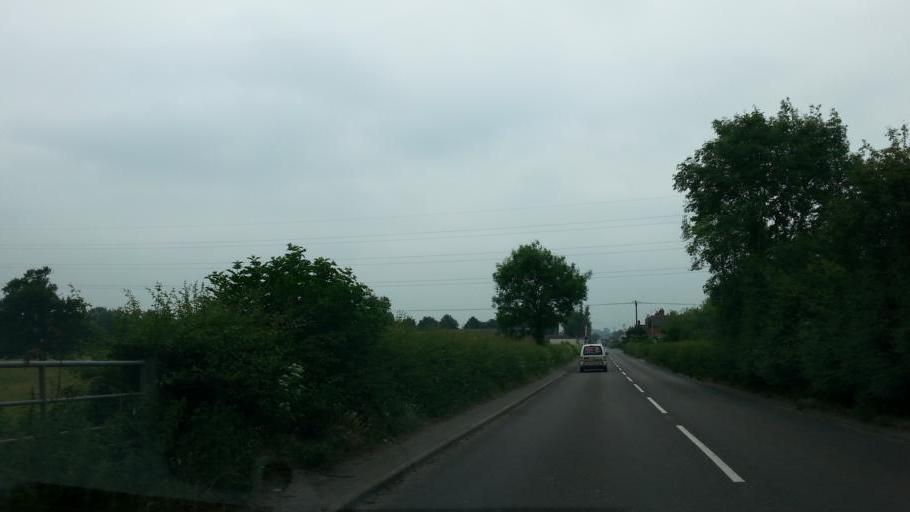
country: GB
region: England
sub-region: Derbyshire
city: Rodsley
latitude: 52.8713
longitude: -1.7606
